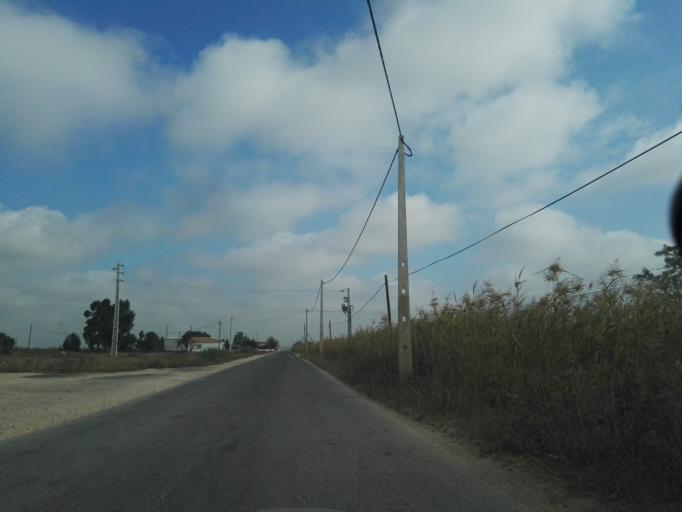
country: PT
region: Santarem
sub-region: Benavente
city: Samora Correia
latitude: 38.9646
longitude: -8.9107
